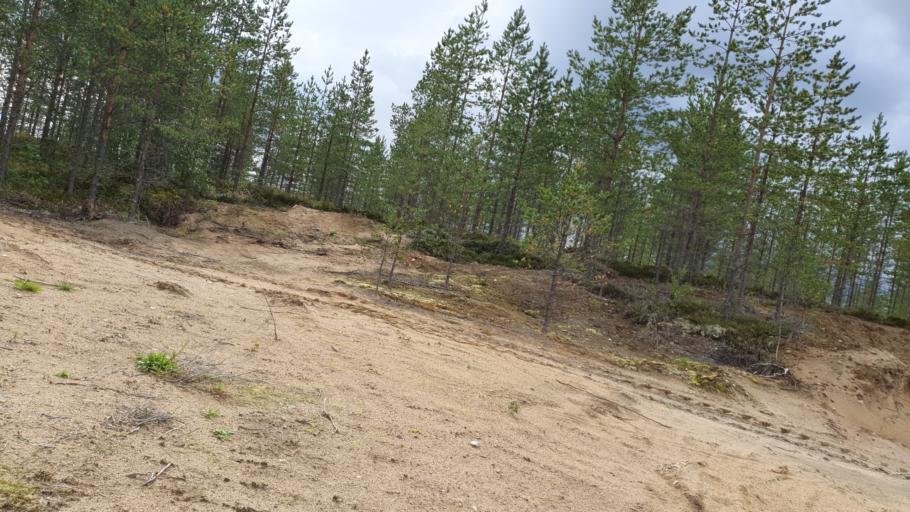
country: FI
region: Kainuu
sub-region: Kehys-Kainuu
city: Kuhmo
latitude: 64.1495
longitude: 29.3668
